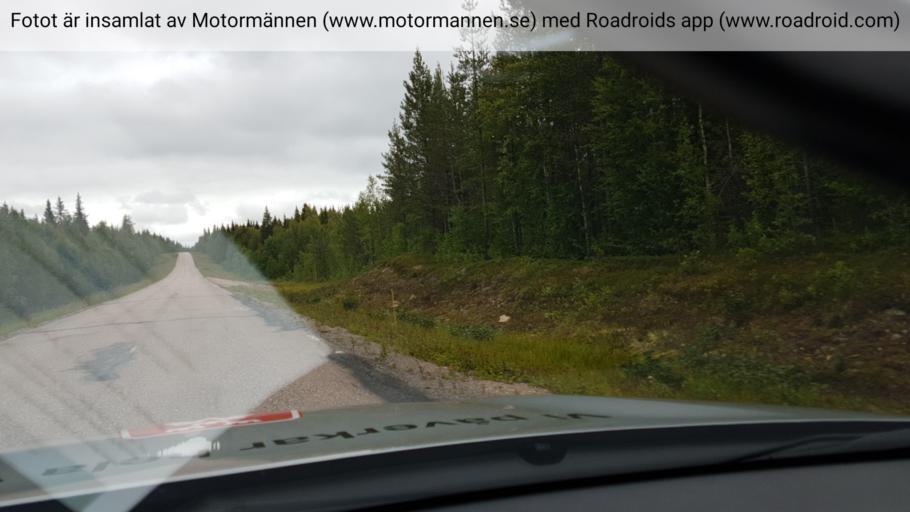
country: SE
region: Norrbotten
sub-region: Overkalix Kommun
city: OEverkalix
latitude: 67.0373
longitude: 22.0309
